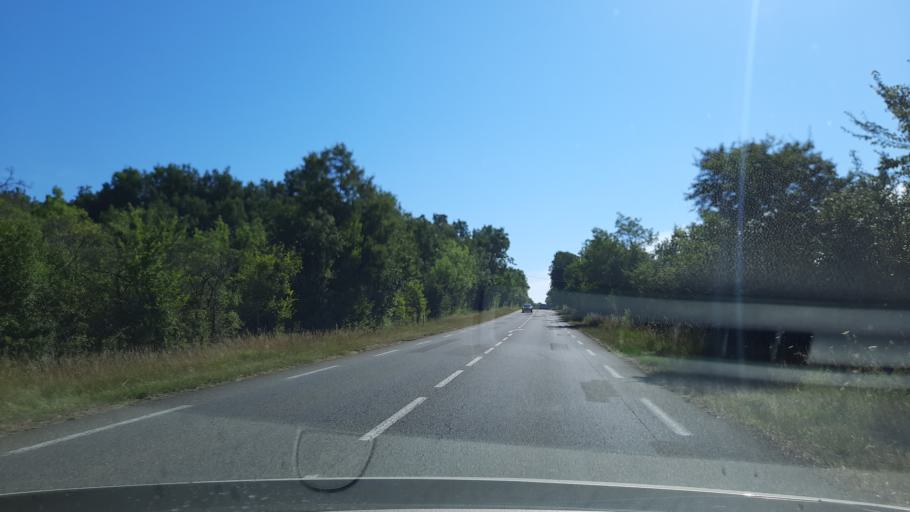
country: FR
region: Midi-Pyrenees
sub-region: Departement du Tarn-et-Garonne
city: Monteils
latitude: 44.1695
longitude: 1.5838
